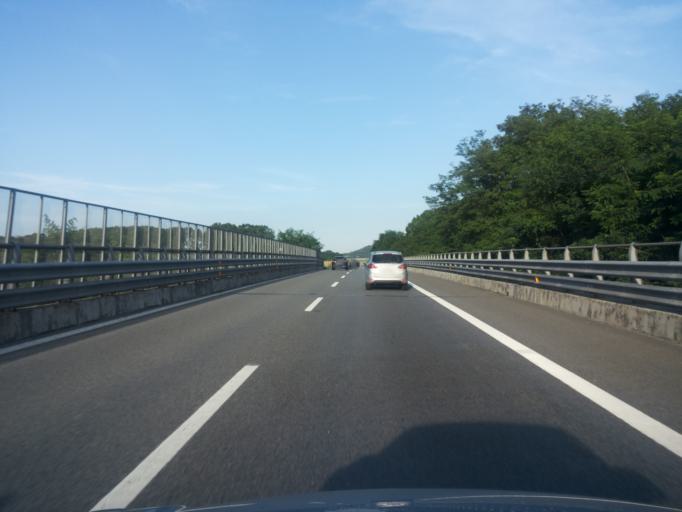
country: IT
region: Piedmont
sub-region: Provincia di Torino
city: Caravino
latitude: 45.4185
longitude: 7.9618
